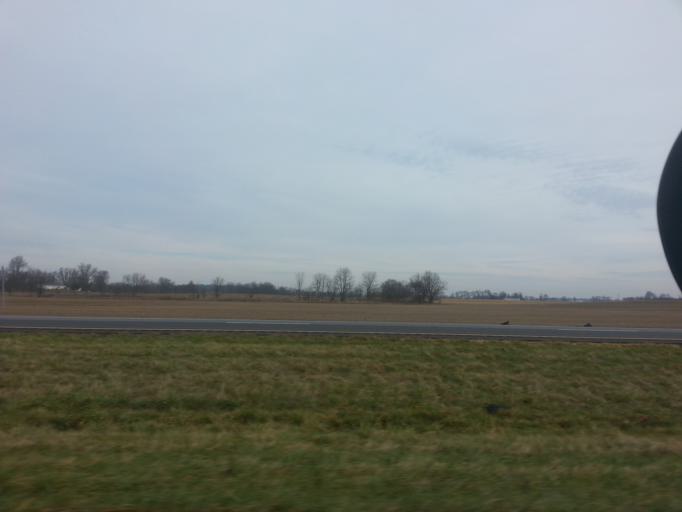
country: US
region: Indiana
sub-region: Montgomery County
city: Crawfordsville
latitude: 40.0994
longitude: -87.0303
